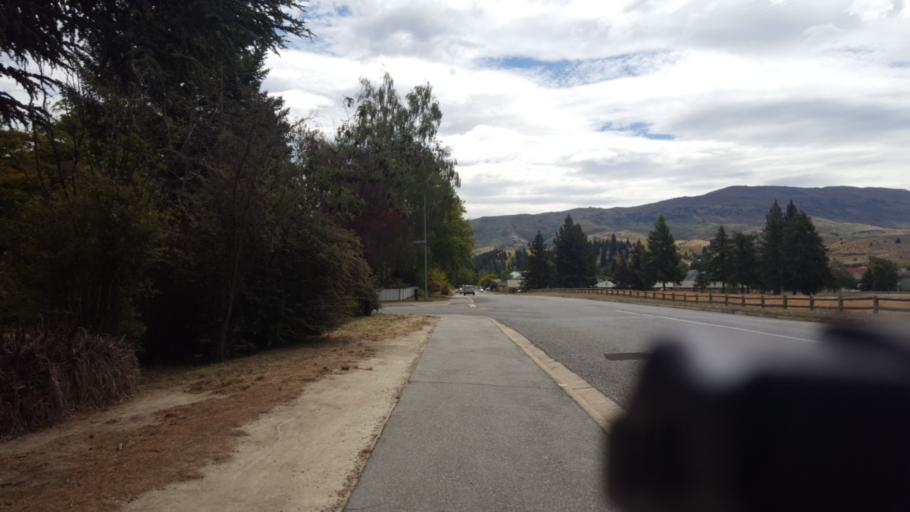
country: NZ
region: Otago
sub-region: Queenstown-Lakes District
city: Wanaka
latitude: -45.0404
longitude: 169.2028
